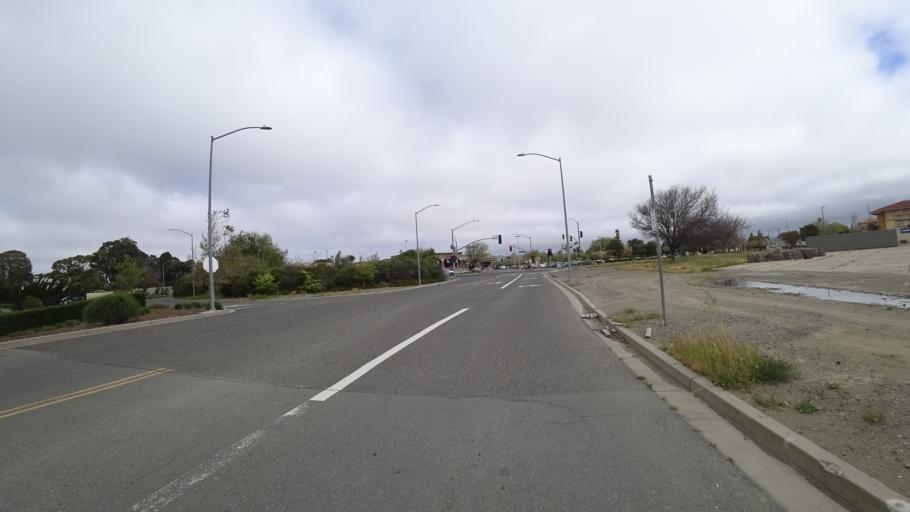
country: US
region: California
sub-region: Alameda County
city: San Lorenzo
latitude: 37.6642
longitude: -122.1202
